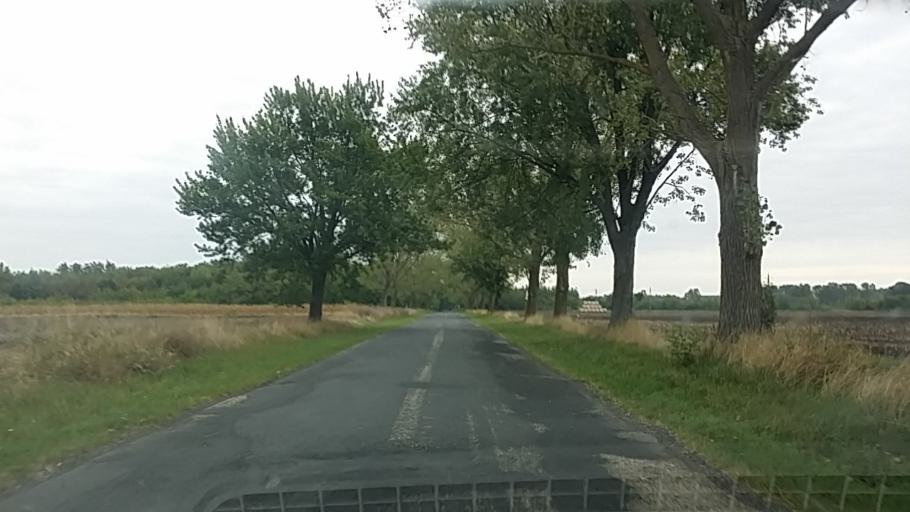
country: HU
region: Gyor-Moson-Sopron
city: Farad
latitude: 47.6529
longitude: 17.1169
